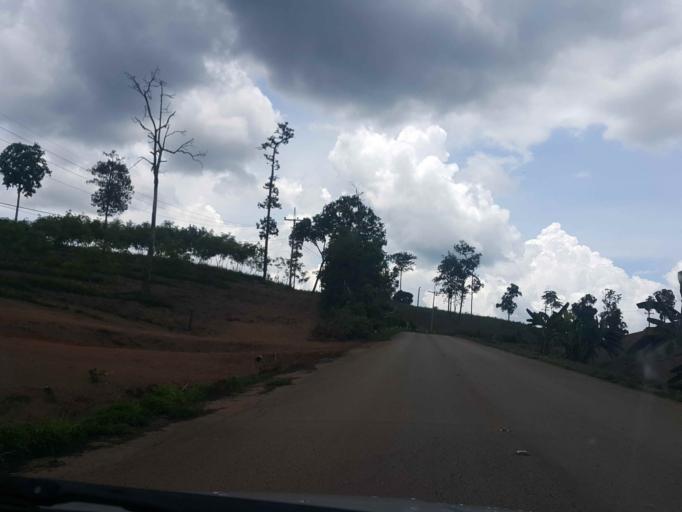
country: TH
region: Lampang
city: Ngao
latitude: 18.9490
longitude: 100.0776
